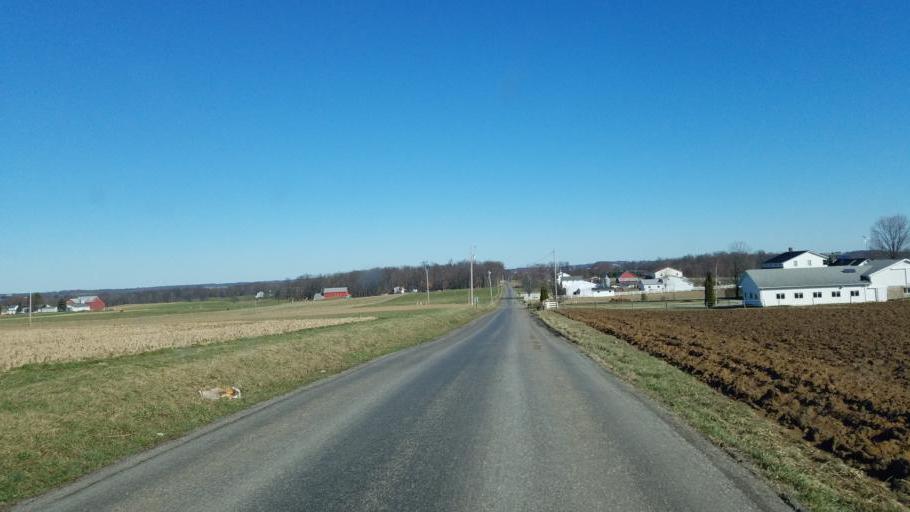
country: US
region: Ohio
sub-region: Wayne County
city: Apple Creek
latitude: 40.6513
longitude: -81.8418
